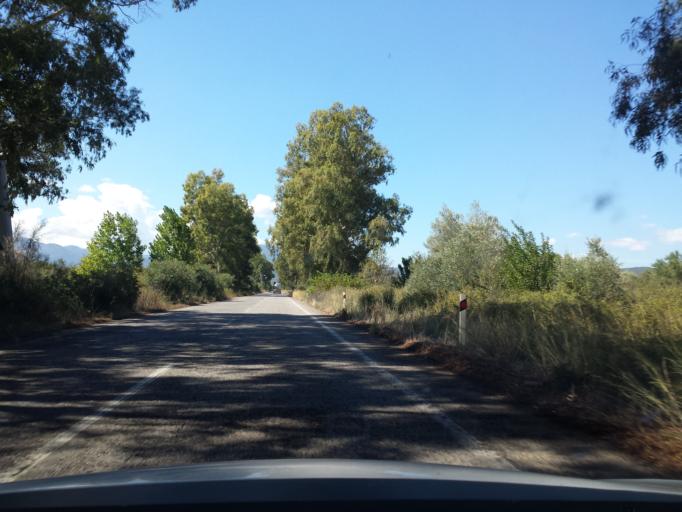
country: GR
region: Peloponnese
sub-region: Nomos Messinias
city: Meligalas
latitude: 37.2549
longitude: 21.9850
